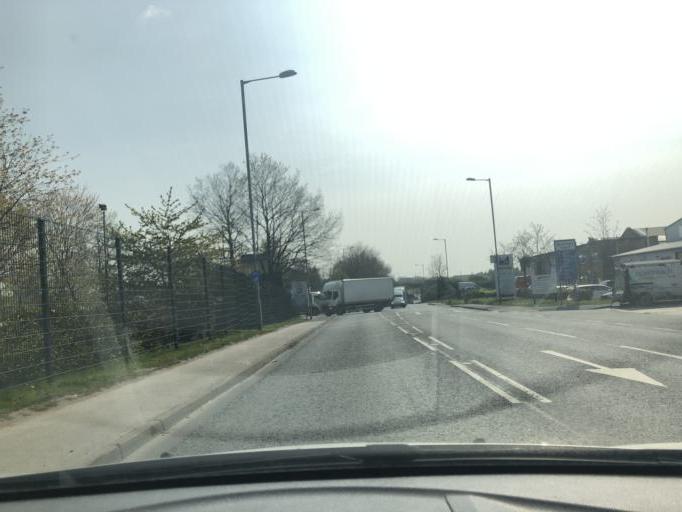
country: GB
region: England
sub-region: Borough of Stockport
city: Bredbury
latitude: 53.4288
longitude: -2.1208
